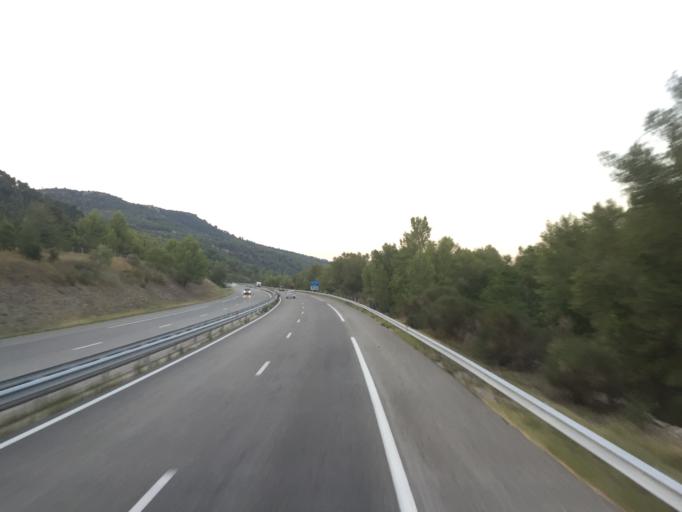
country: FR
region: Provence-Alpes-Cote d'Azur
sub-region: Departement des Alpes-de-Haute-Provence
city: Oraison
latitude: 43.9763
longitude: 5.9100
